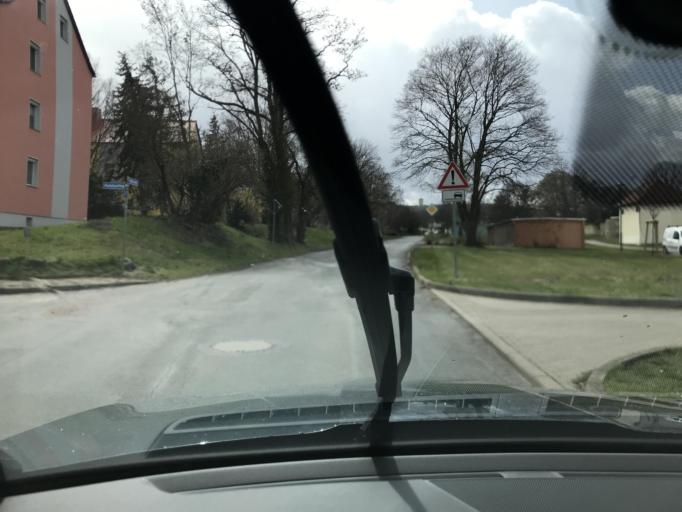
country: DE
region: Saxony-Anhalt
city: Ballenstedt
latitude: 51.7220
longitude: 11.2472
